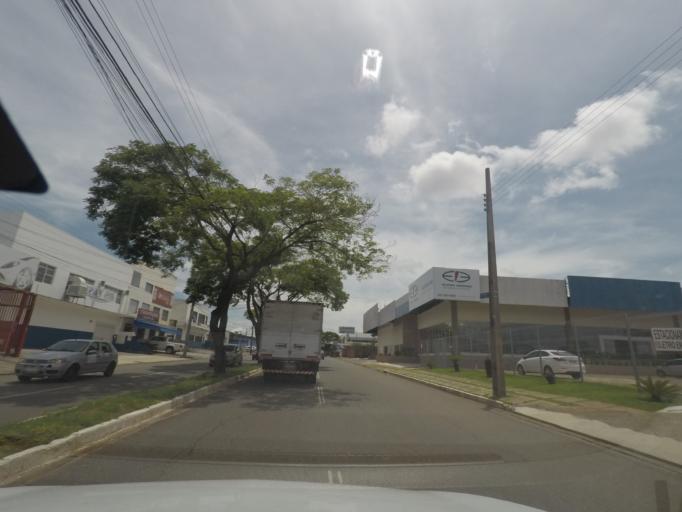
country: BR
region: Goias
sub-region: Goiania
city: Goiania
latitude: -16.6855
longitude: -49.2952
